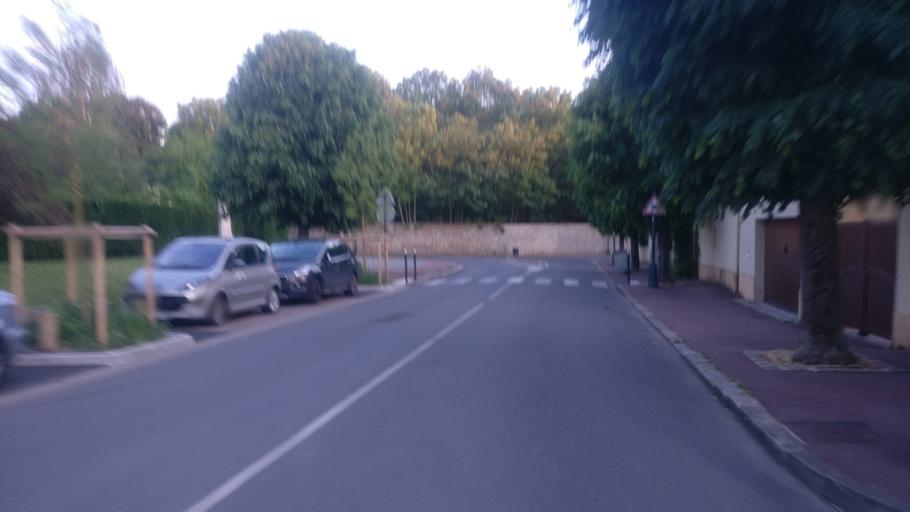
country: FR
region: Ile-de-France
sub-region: Departement du Val-de-Marne
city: Santeny
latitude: 48.7365
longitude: 2.5544
